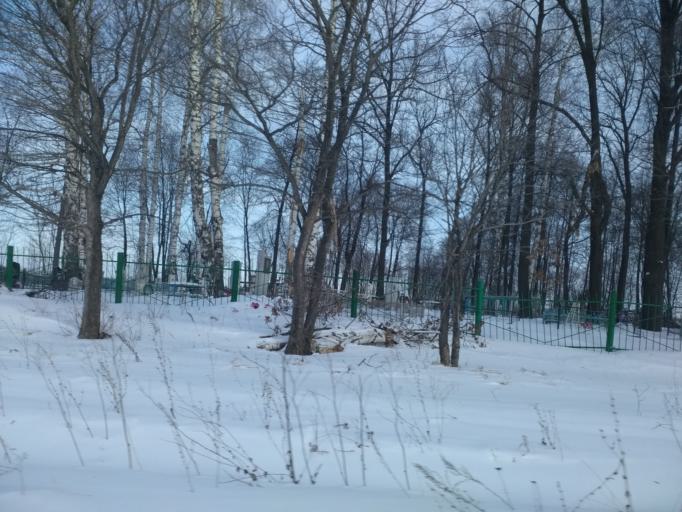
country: RU
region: Bashkortostan
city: Iglino
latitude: 54.7718
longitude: 56.5477
